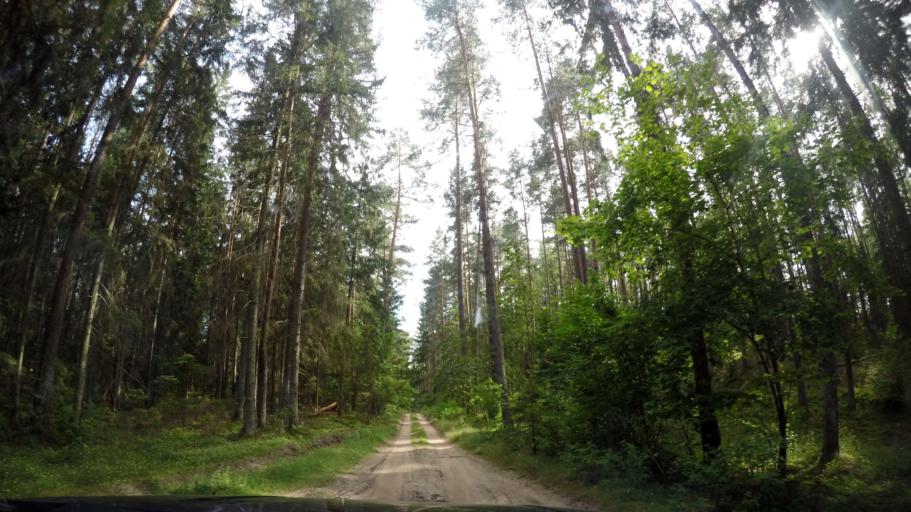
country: BY
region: Grodnenskaya
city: Skidal'
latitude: 53.8384
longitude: 24.1766
